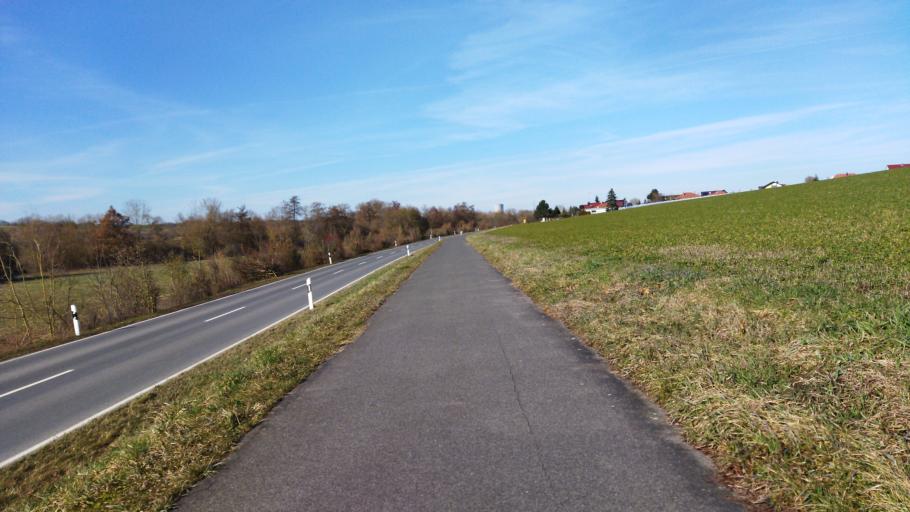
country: DE
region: Bavaria
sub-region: Regierungsbezirk Unterfranken
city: Wipfeld
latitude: 49.9366
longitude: 10.1825
